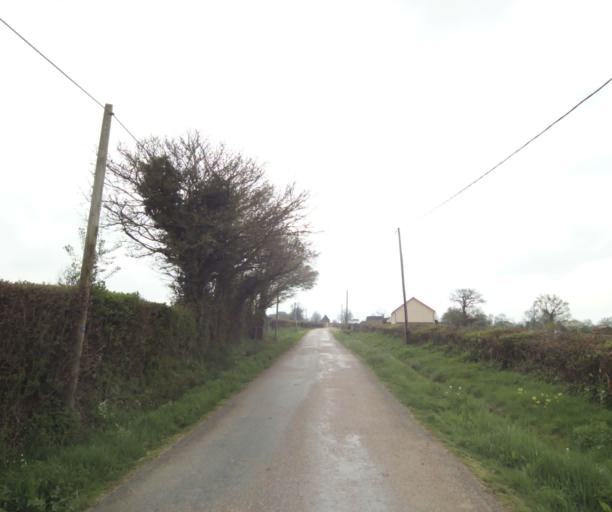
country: FR
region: Bourgogne
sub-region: Departement de Saone-et-Loire
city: Charolles
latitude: 46.3603
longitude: 4.2178
